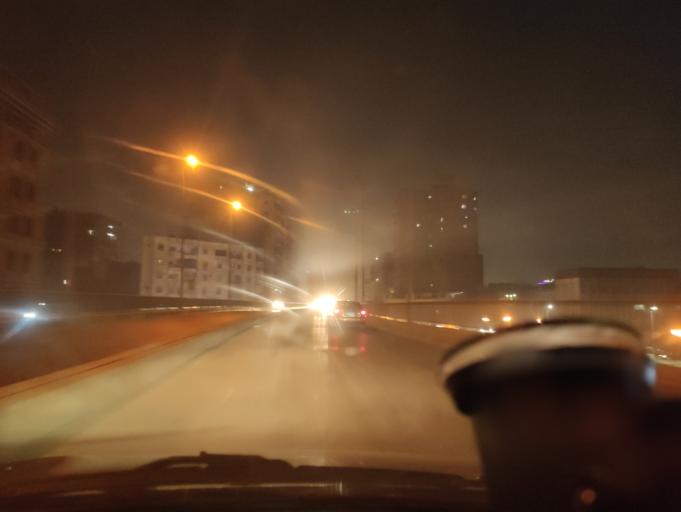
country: EG
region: Muhafazat al Qahirah
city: Cairo
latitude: 30.0933
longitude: 31.2752
